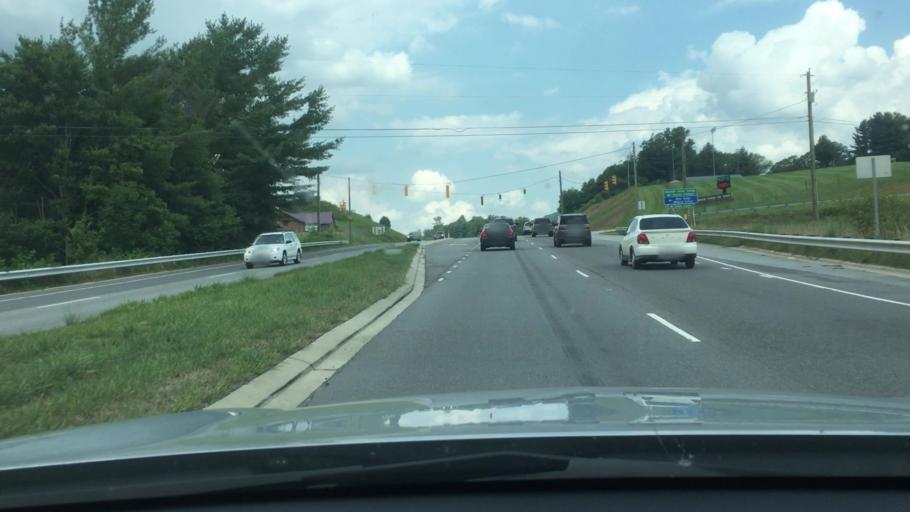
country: US
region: North Carolina
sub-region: Yancey County
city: Burnsville
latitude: 35.9127
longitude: -82.3354
